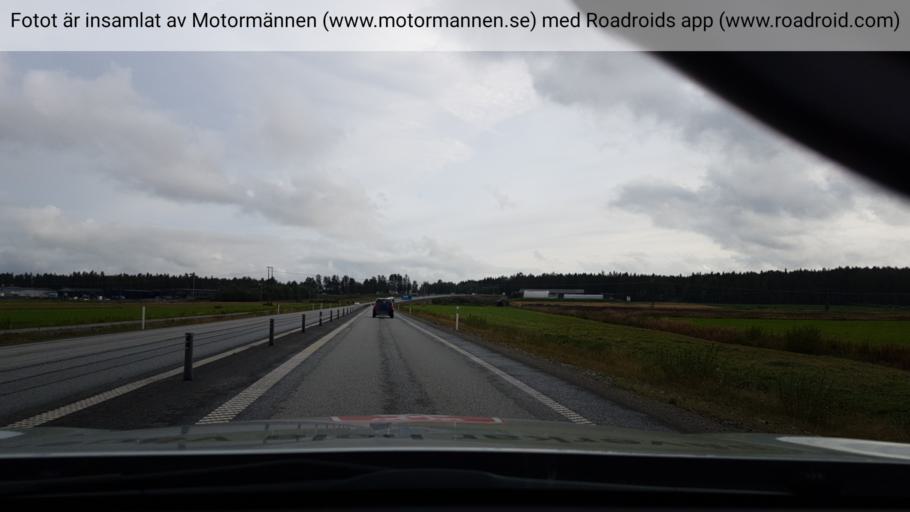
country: SE
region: Vaesterbotten
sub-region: Umea Kommun
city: Roback
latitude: 63.8486
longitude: 20.1906
